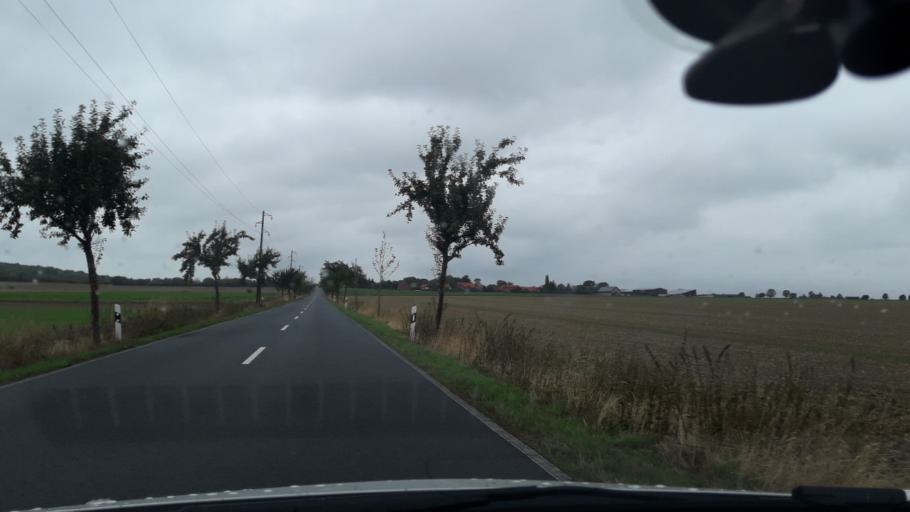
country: DE
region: Lower Saxony
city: Schladen
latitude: 51.9832
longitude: 10.5359
